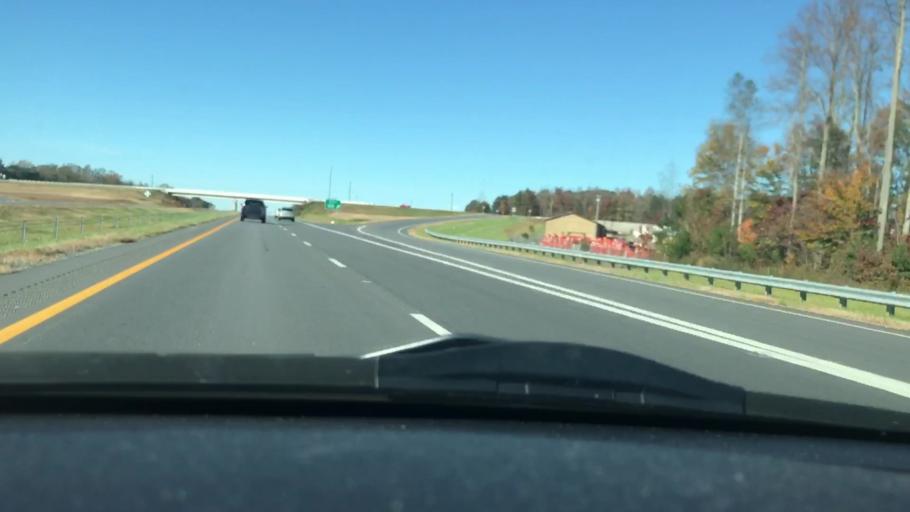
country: US
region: North Carolina
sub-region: Guilford County
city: Stokesdale
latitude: 36.2645
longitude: -79.9287
